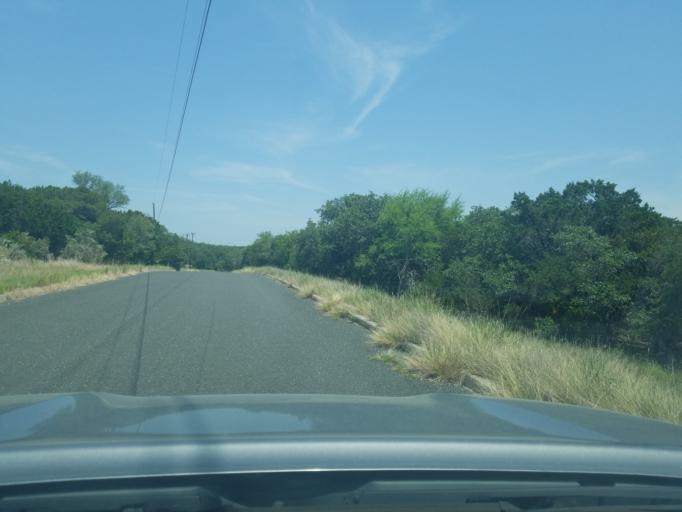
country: US
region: Texas
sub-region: Bexar County
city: Timberwood Park
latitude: 29.6750
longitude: -98.5016
